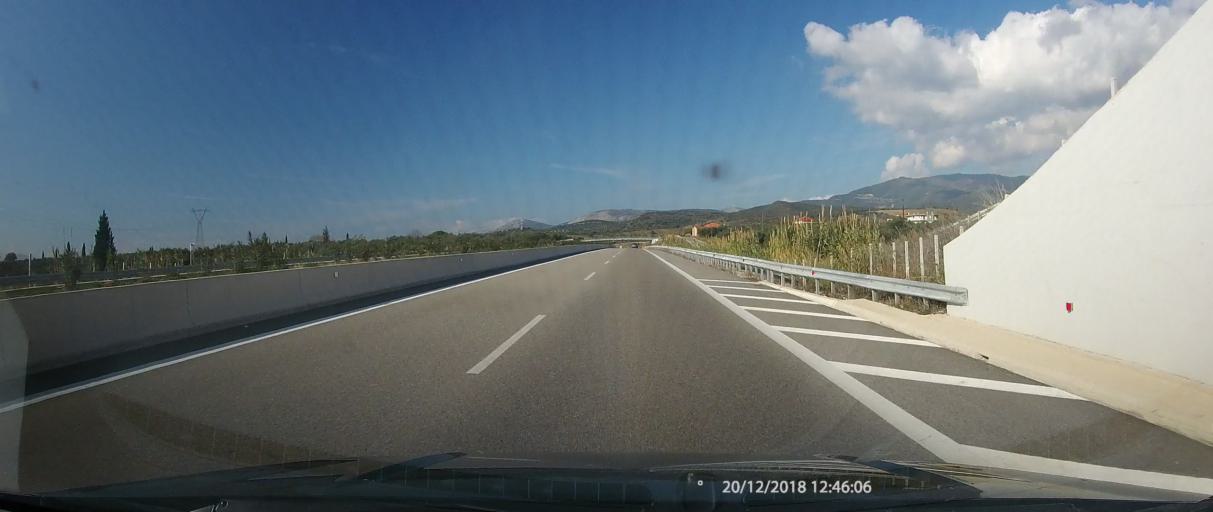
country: GR
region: West Greece
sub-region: Nomos Aitolias kai Akarnanias
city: Mesolongi
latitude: 38.3885
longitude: 21.4809
